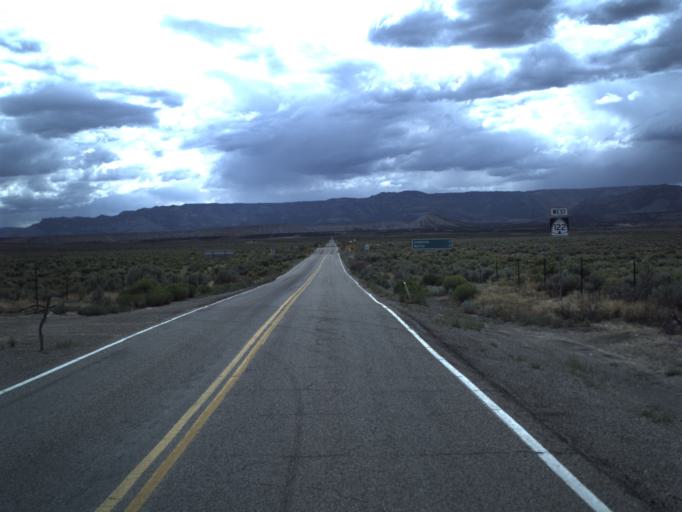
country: US
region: Utah
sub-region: Carbon County
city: Price
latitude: 39.4933
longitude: -110.8461
